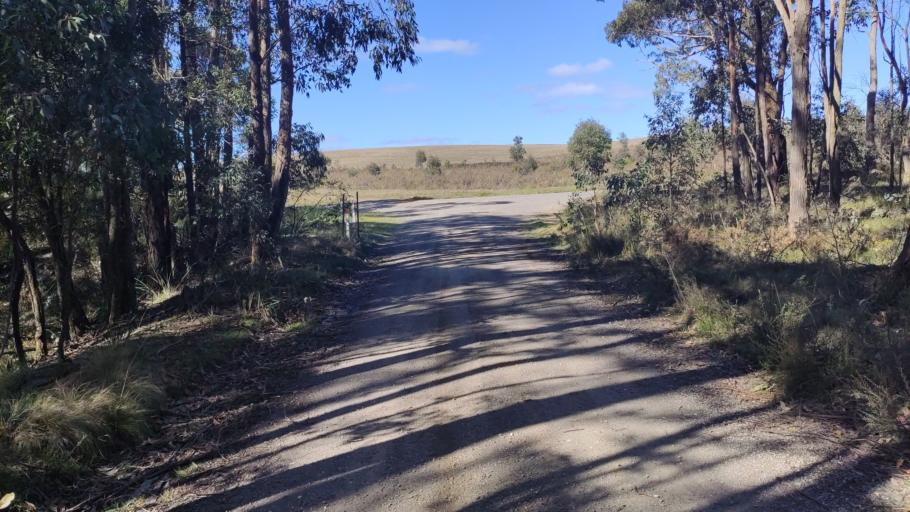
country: AU
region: Victoria
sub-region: Ballarat North
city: Delacombe
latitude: -37.7389
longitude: 143.7520
